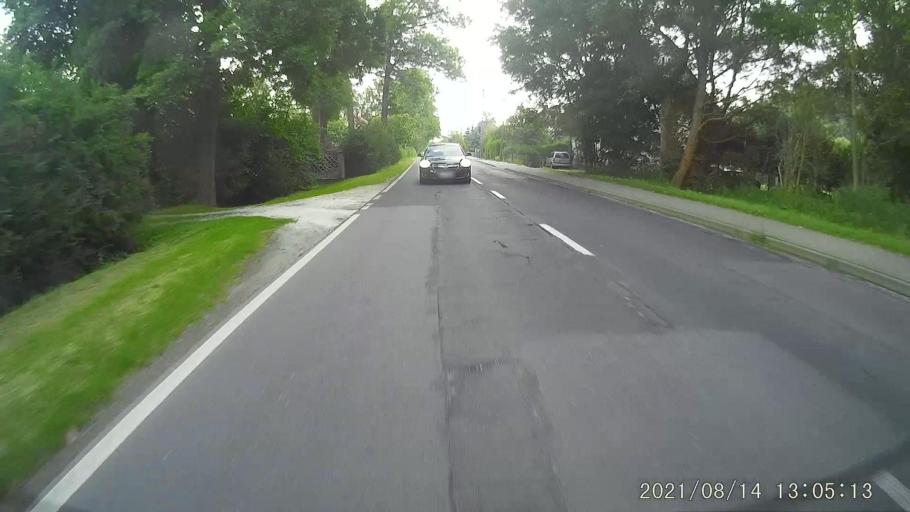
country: PL
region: Lower Silesian Voivodeship
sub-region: Powiat klodzki
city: Bystrzyca Klodzka
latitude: 50.3559
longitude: 16.7285
